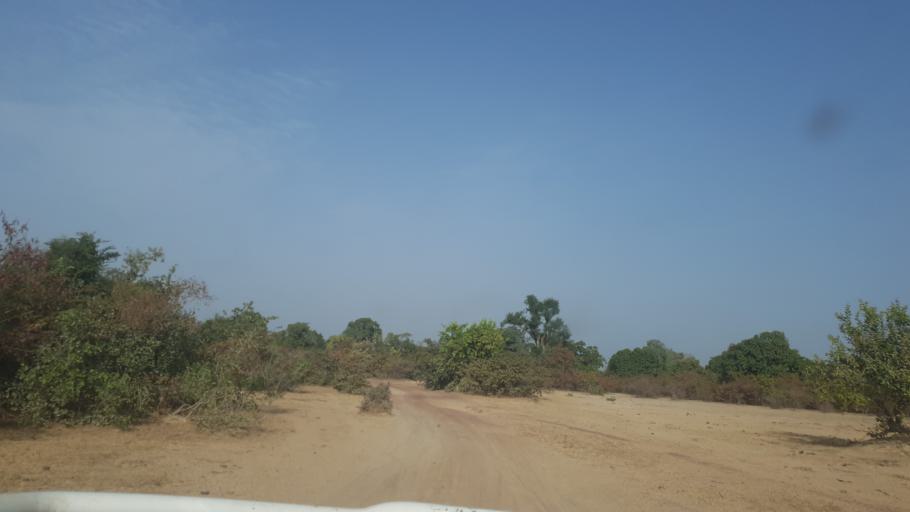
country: ML
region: Segou
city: Baroueli
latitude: 13.3643
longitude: -6.9195
